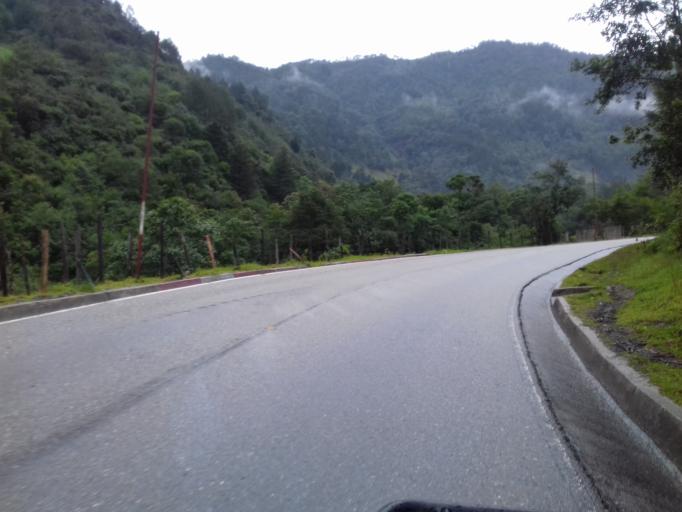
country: GT
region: Quiche
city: Nebaj
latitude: 15.3867
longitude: -91.1133
